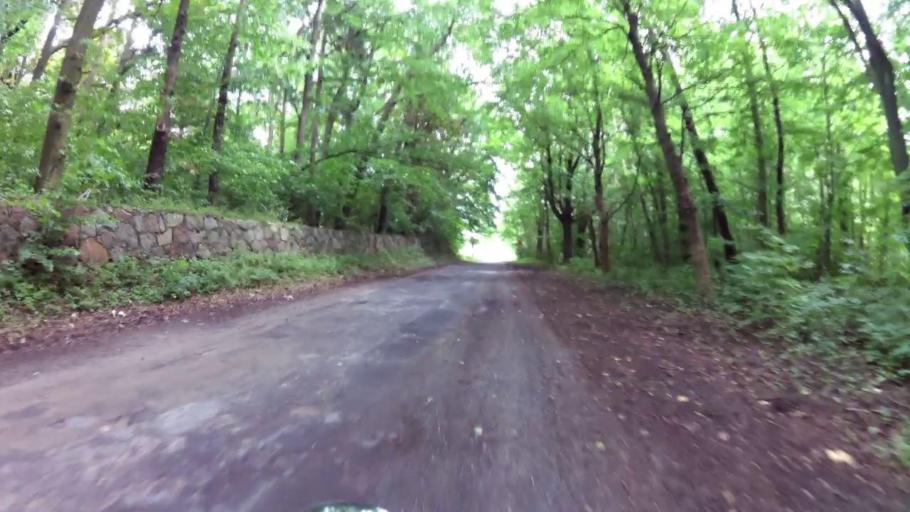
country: PL
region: West Pomeranian Voivodeship
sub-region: Powiat bialogardzki
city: Karlino
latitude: 54.0597
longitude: 15.8415
